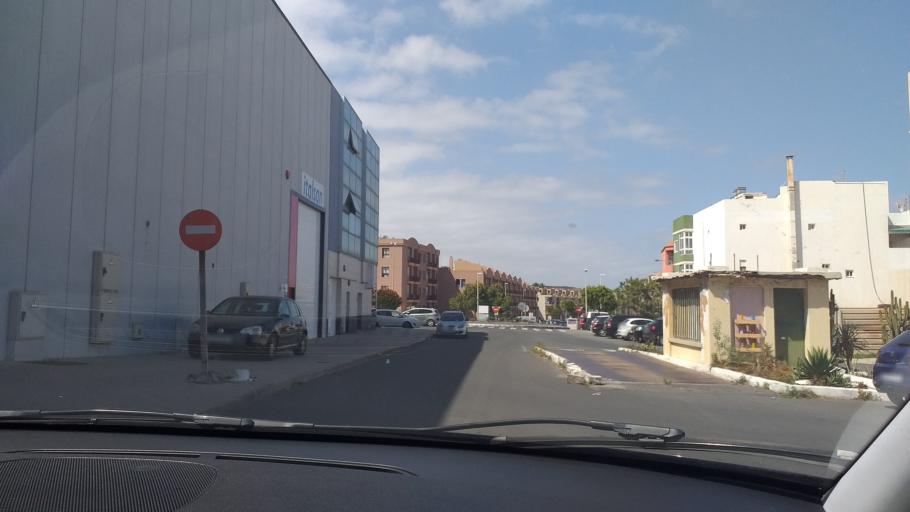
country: ES
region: Canary Islands
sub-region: Provincia de Las Palmas
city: Telde
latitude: 27.9799
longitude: -15.3781
